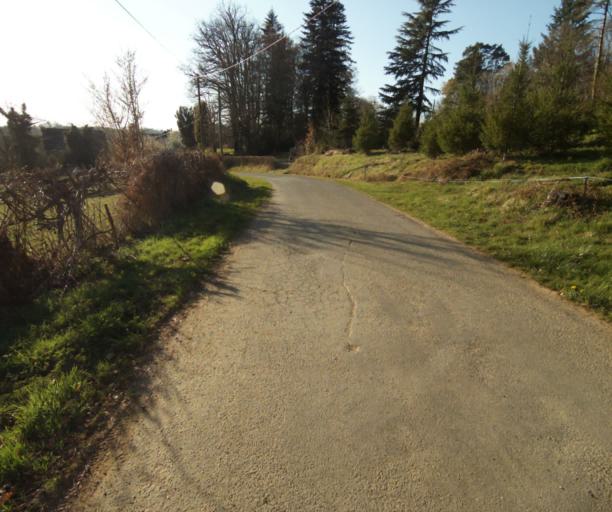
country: FR
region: Limousin
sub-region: Departement de la Correze
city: Saint-Clement
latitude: 45.3525
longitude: 1.6789
